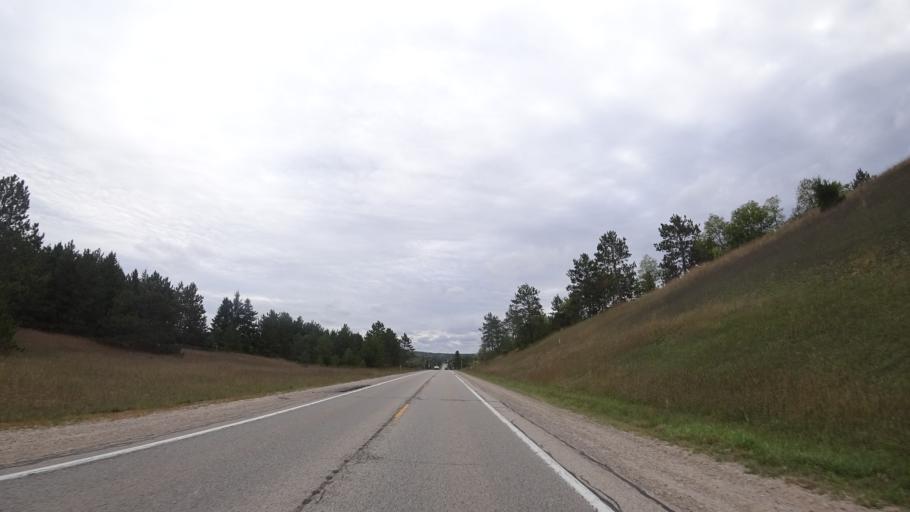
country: US
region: Michigan
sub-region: Charlevoix County
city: Boyne City
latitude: 45.1876
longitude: -84.9149
